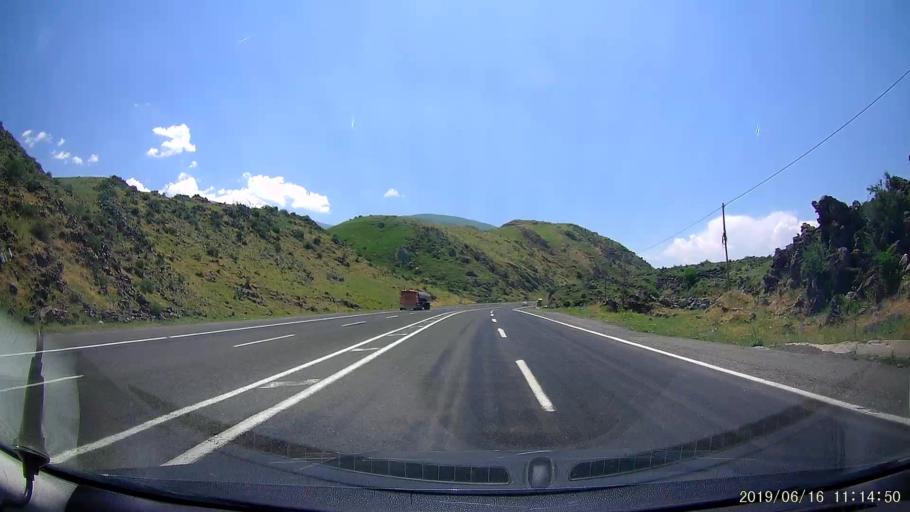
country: TR
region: Igdir
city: Igdir
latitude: 39.7726
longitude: 44.1424
